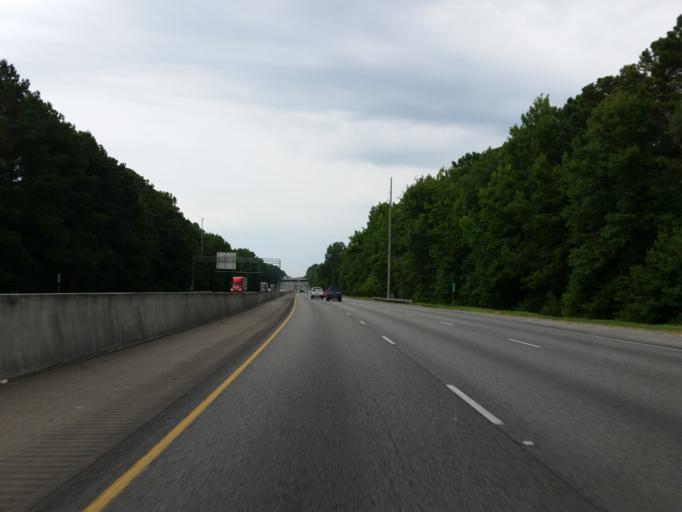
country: US
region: Georgia
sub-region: Bibb County
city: West Point
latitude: 32.9437
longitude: -83.8118
